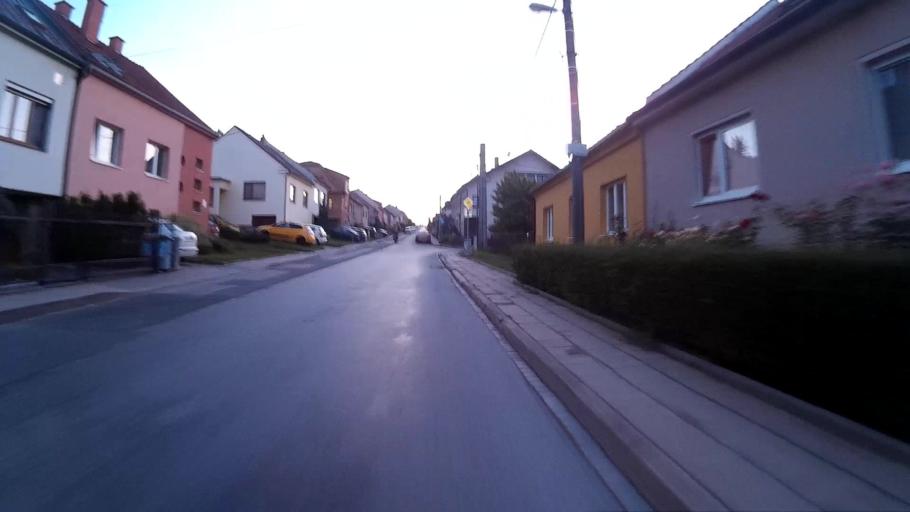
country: CZ
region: South Moravian
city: Troubsko
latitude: 49.1757
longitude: 16.5258
